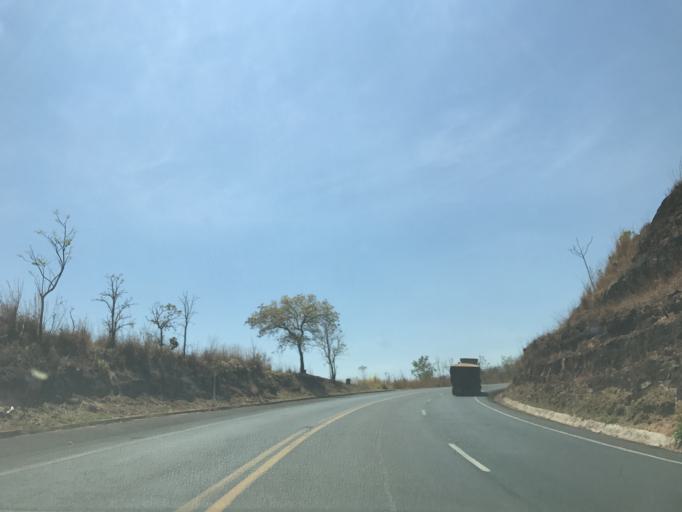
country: BR
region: Minas Gerais
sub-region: Frutal
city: Frutal
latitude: -19.8693
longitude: -48.9723
